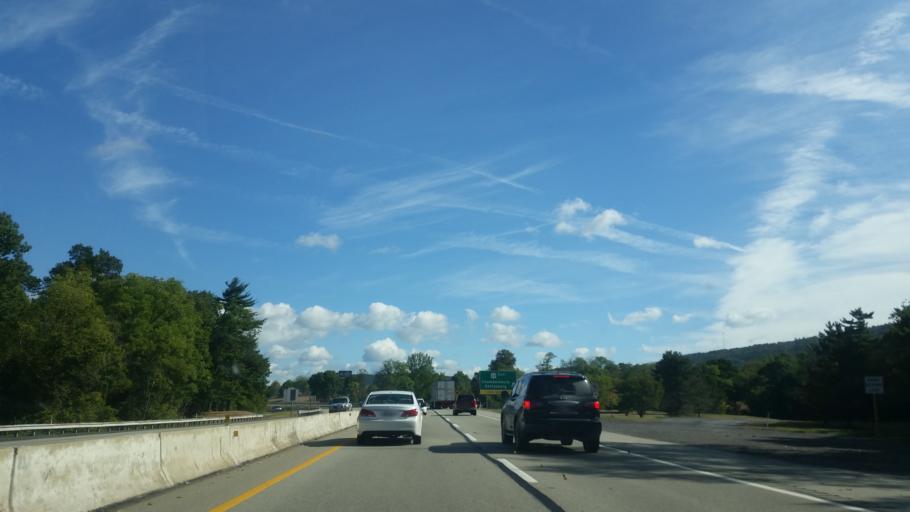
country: US
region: Pennsylvania
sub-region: Bedford County
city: Earlston
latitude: 39.9939
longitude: -78.2352
